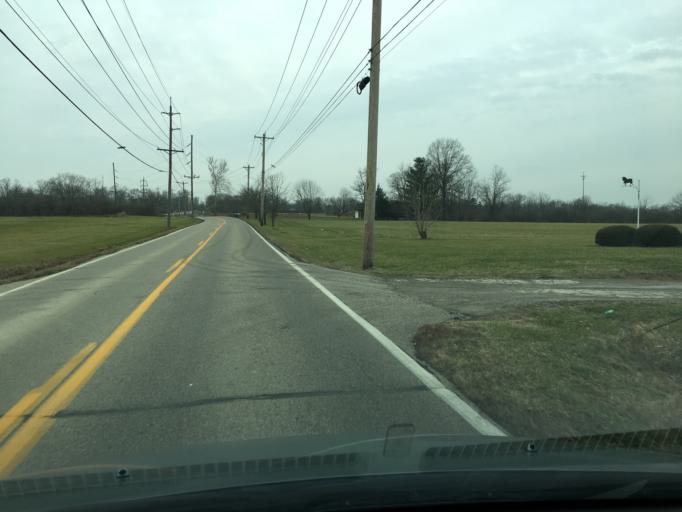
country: US
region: Ohio
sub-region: Hamilton County
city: Highpoint
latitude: 39.3177
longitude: -84.3538
